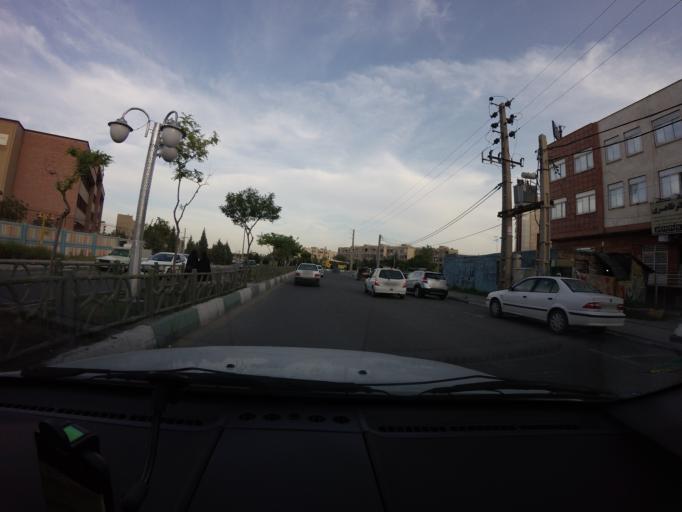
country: IR
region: Tehran
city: Eslamshahr
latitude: 35.5267
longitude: 51.2284
